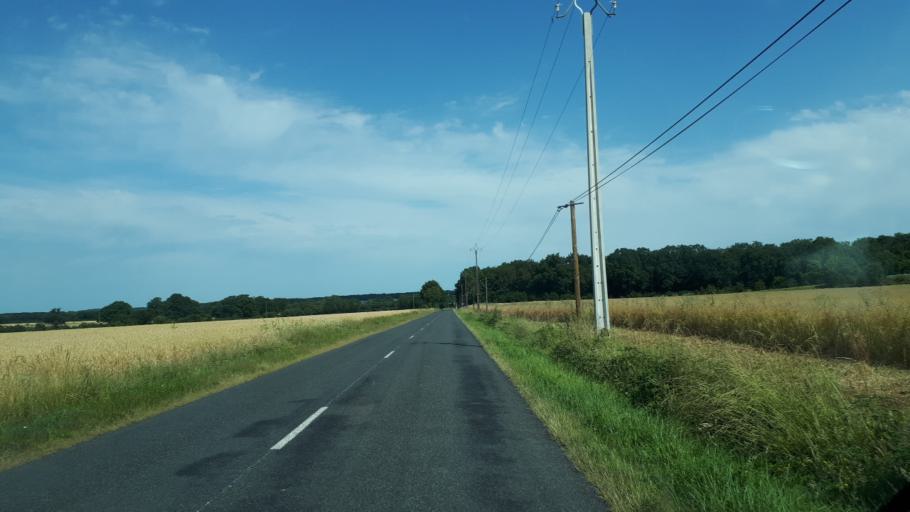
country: FR
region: Centre
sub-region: Departement du Loir-et-Cher
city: Droue
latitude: 47.9785
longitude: 1.0452
